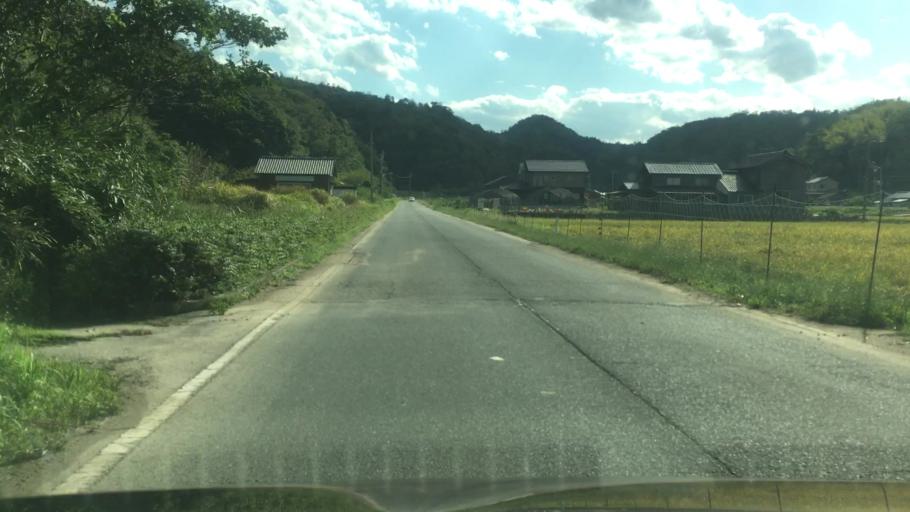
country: JP
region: Hyogo
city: Toyooka
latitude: 35.6492
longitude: 134.9658
